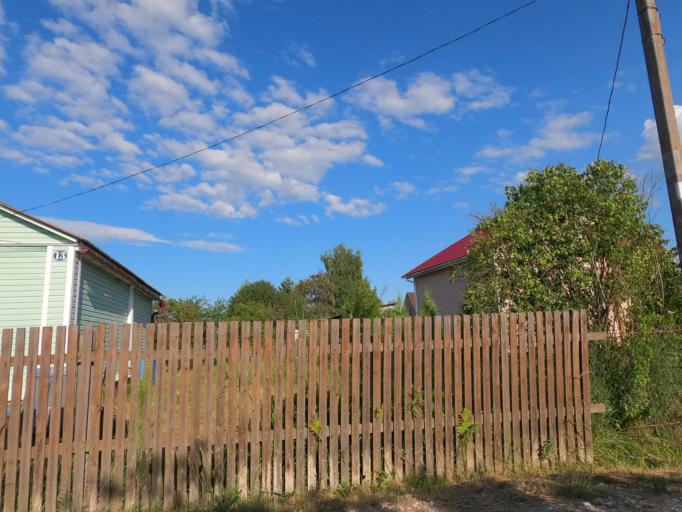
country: RU
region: Moskovskaya
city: Konobeyevo
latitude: 55.4085
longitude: 38.7175
